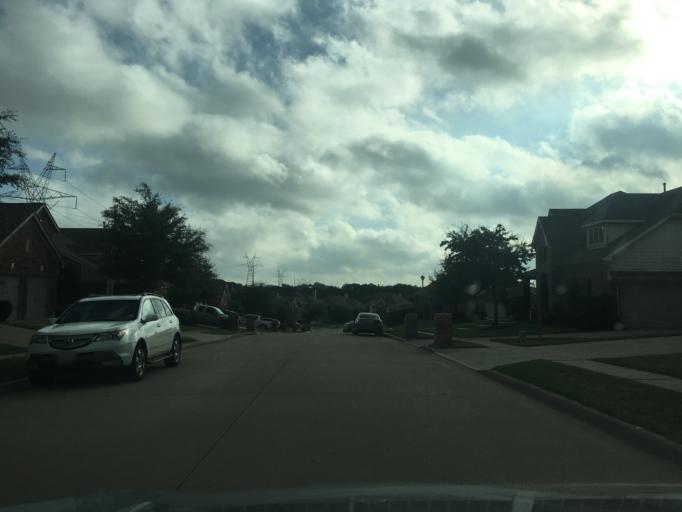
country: US
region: Texas
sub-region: Dallas County
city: Sachse
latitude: 32.9631
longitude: -96.5968
